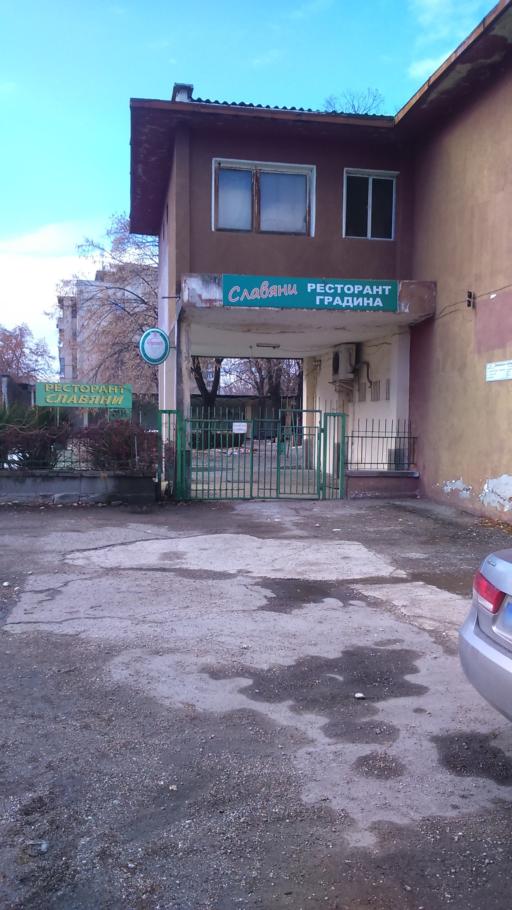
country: BG
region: Plovdiv
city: Stamboliyski
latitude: 42.1323
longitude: 24.5389
